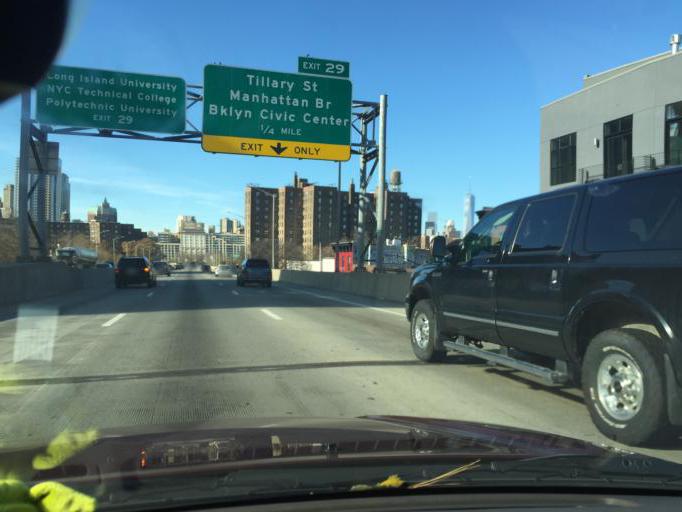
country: US
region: New York
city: New York City
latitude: 40.6962
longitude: -73.9743
